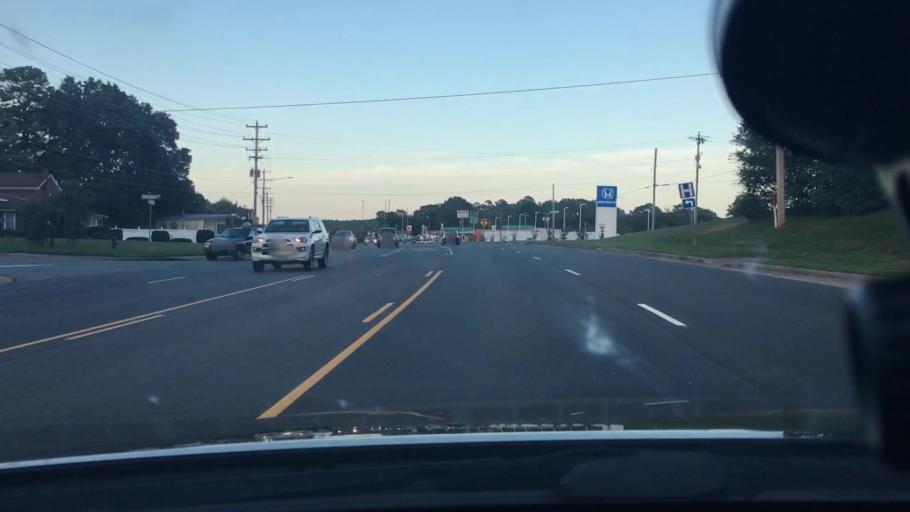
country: US
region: North Carolina
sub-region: Stanly County
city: Albemarle
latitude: 35.3385
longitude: -80.2039
